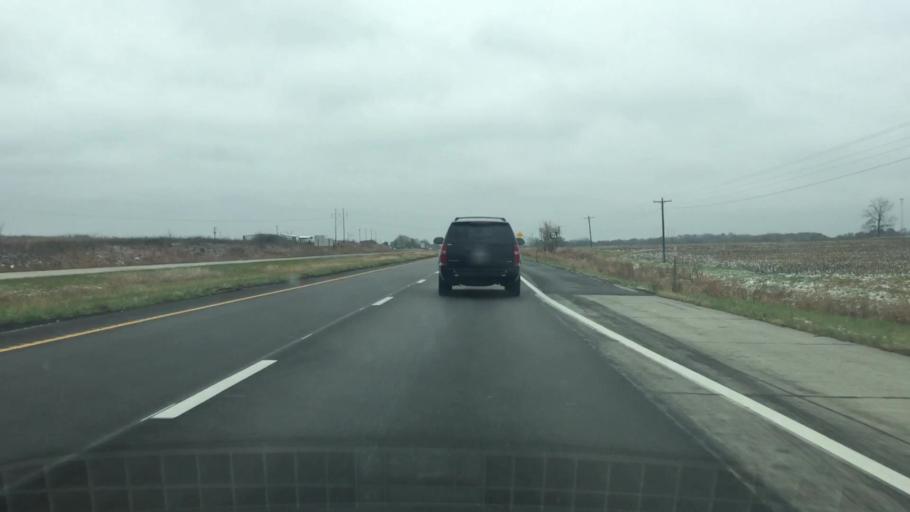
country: US
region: Missouri
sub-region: Saint Clair County
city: Osceola
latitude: 38.0361
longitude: -93.6793
